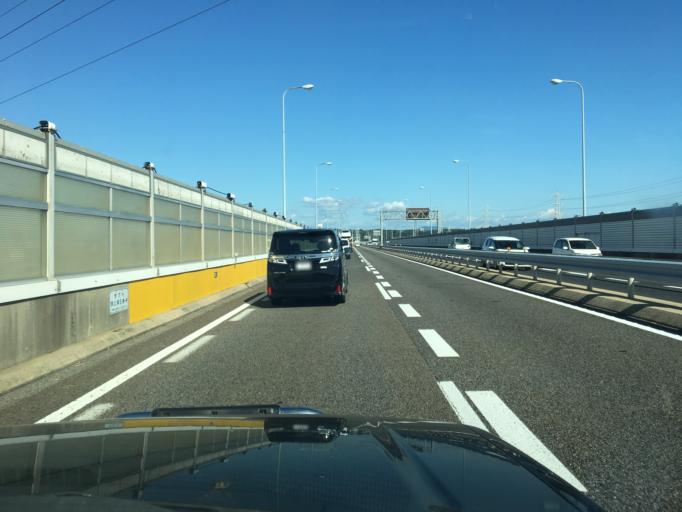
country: JP
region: Aichi
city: Kasugai
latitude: 35.2249
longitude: 136.9575
